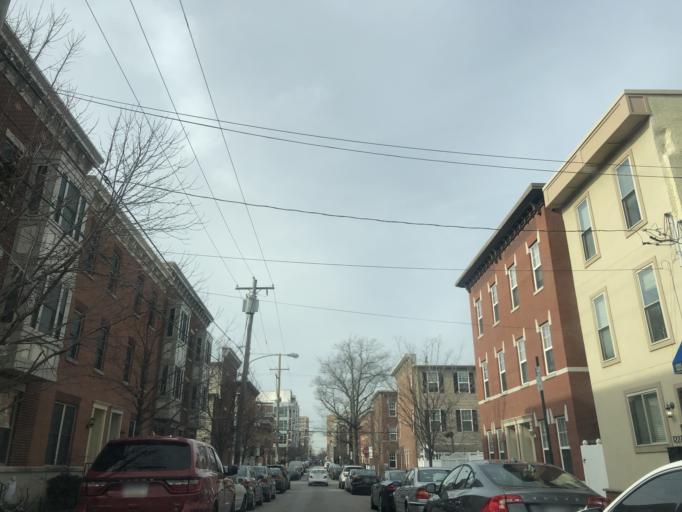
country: US
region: Pennsylvania
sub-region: Philadelphia County
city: Philadelphia
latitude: 39.9415
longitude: -75.1630
